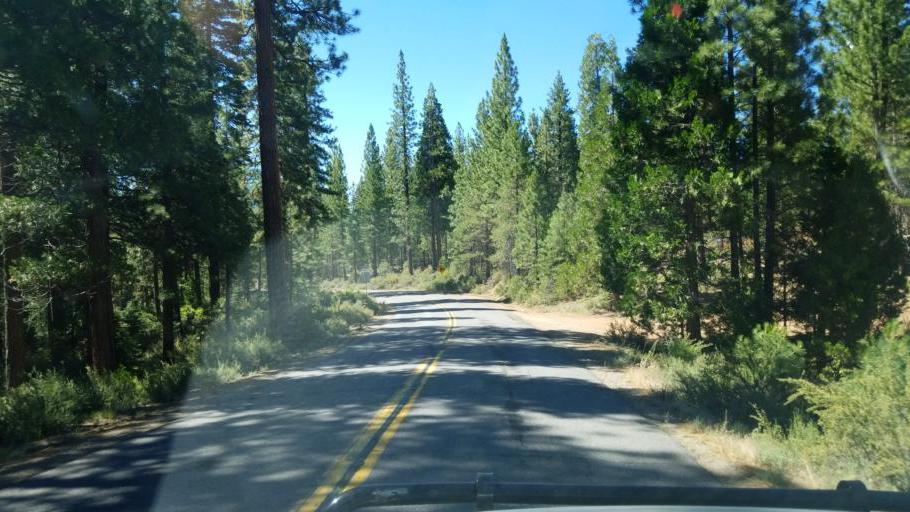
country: US
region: California
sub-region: Lassen County
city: Susanville
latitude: 40.4406
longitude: -120.7481
